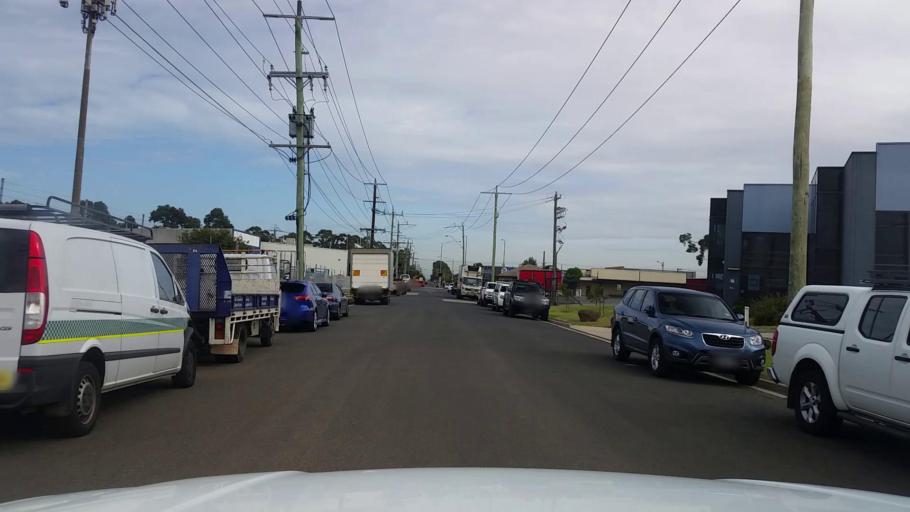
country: AU
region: Victoria
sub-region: Casey
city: Doveton
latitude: -38.0000
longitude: 145.2202
